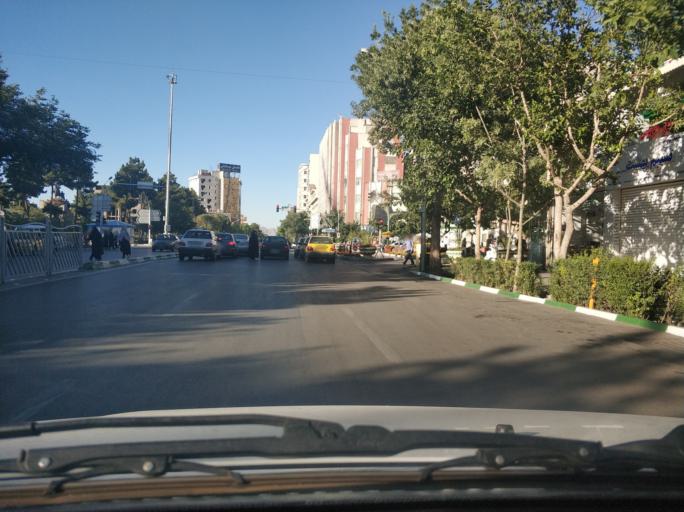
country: IR
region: Razavi Khorasan
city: Mashhad
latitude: 36.2935
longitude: 59.6097
